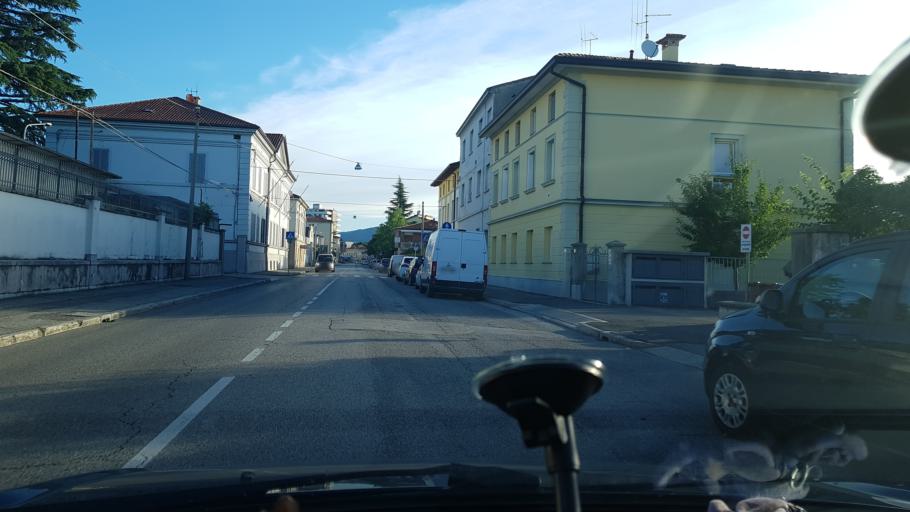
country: IT
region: Friuli Venezia Giulia
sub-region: Provincia di Gorizia
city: Gorizia
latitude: 45.9321
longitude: 13.6131
